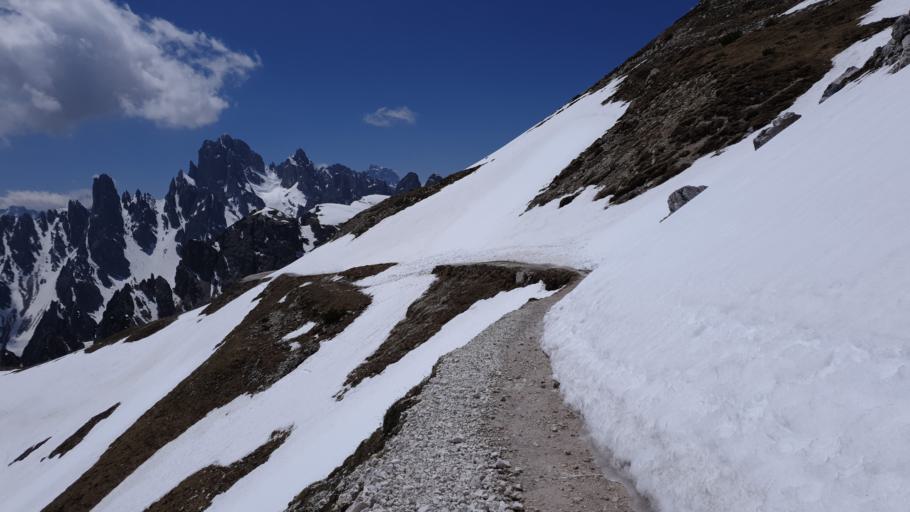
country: IT
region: Trentino-Alto Adige
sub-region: Bolzano
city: Sesto
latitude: 46.6154
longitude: 12.3092
